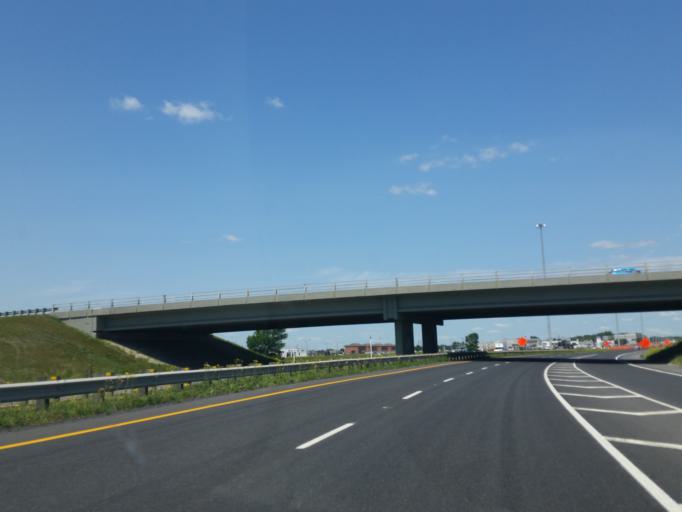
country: CA
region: Quebec
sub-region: Monteregie
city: Saint-Jean-sur-Richelieu
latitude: 45.3305
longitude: -73.2870
